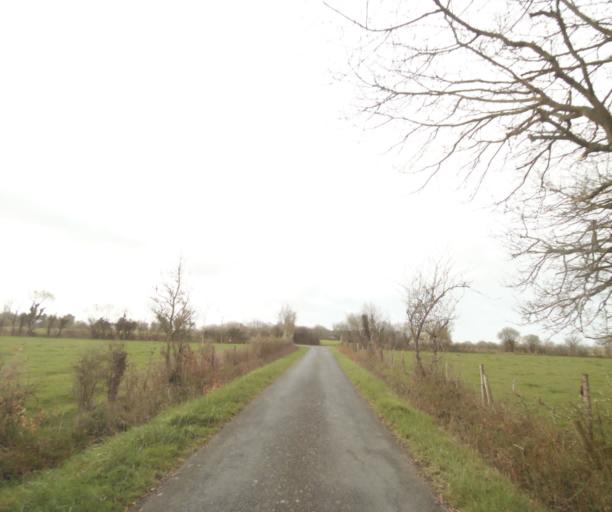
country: FR
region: Pays de la Loire
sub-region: Departement de la Loire-Atlantique
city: Bouvron
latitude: 47.4016
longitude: -1.8726
